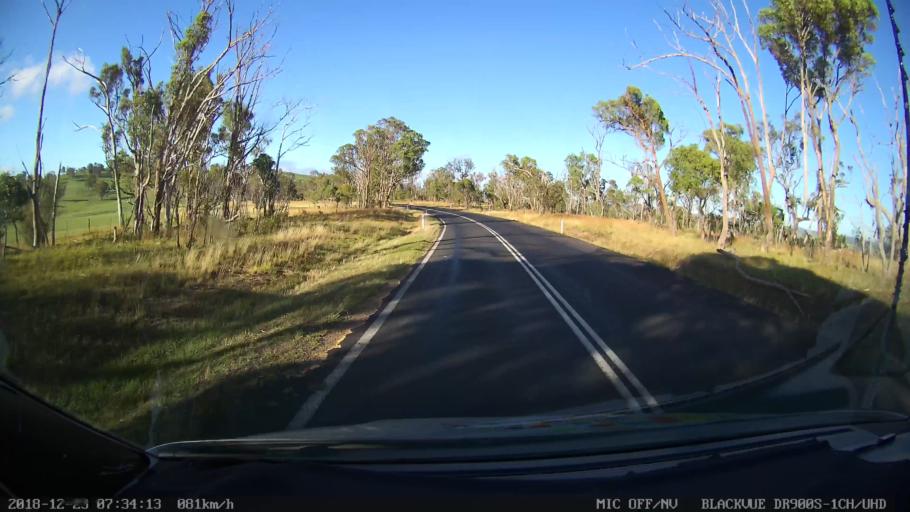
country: AU
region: New South Wales
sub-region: Armidale Dumaresq
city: Enmore
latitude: -30.5181
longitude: 152.0952
